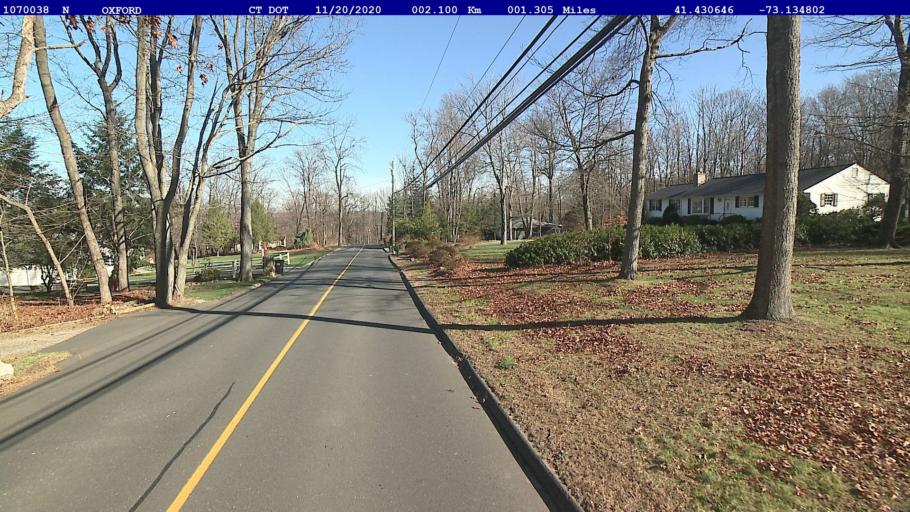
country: US
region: Connecticut
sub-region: New Haven County
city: Oxford
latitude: 41.4306
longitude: -73.1348
